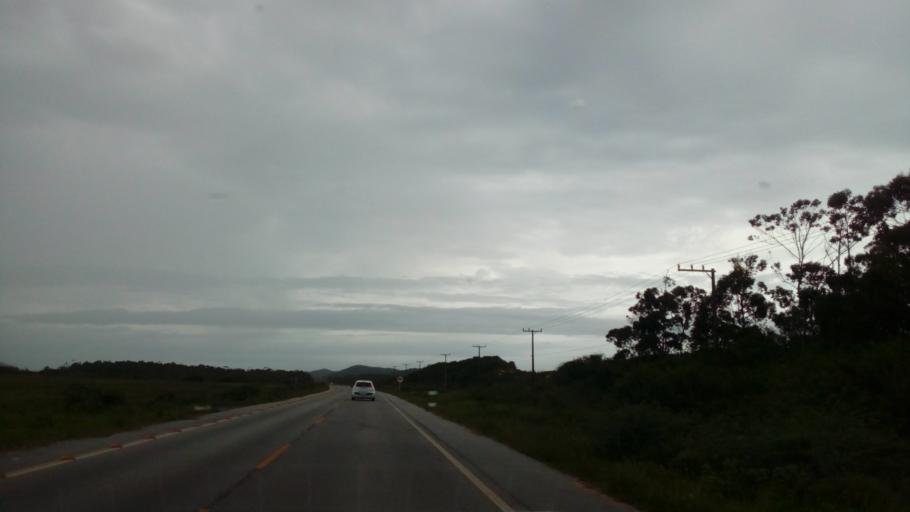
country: BR
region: Santa Catarina
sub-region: Laguna
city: Laguna
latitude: -28.5454
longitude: -48.7927
